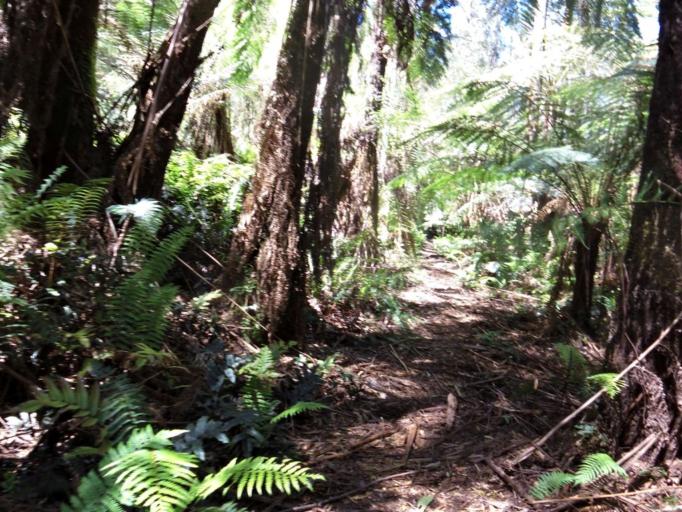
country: AU
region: Victoria
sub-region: Yarra Ranges
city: Millgrove
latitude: -37.8583
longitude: 145.7619
